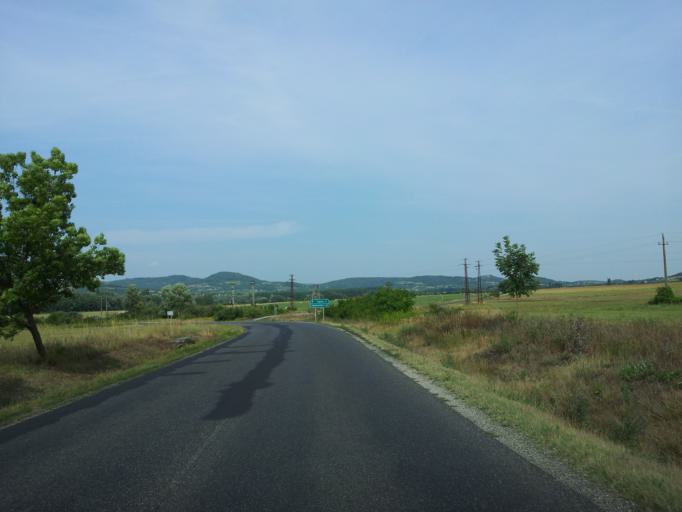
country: HU
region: Veszprem
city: Badacsonytomaj
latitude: 46.8423
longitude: 17.4923
